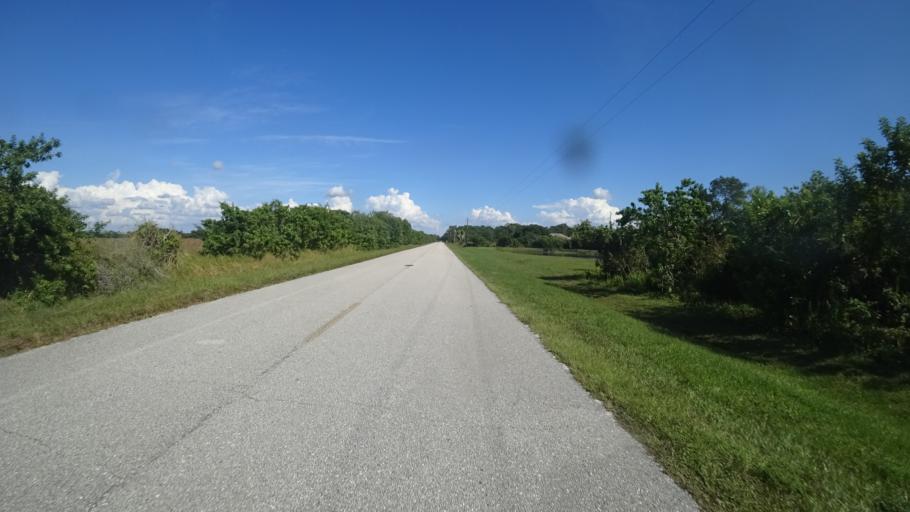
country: US
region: Florida
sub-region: Sarasota County
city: The Meadows
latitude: 27.4305
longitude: -82.2821
